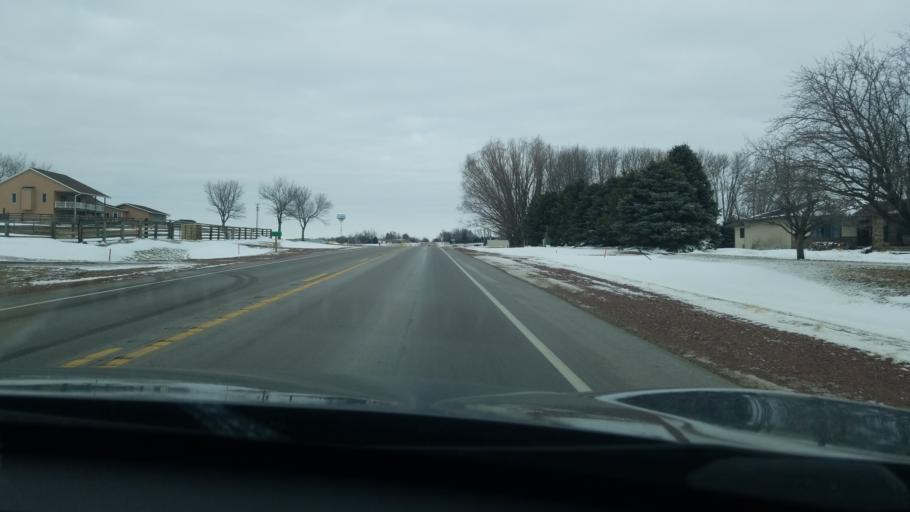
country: US
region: South Dakota
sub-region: Minnehaha County
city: Brandon
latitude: 43.4389
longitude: -96.4292
